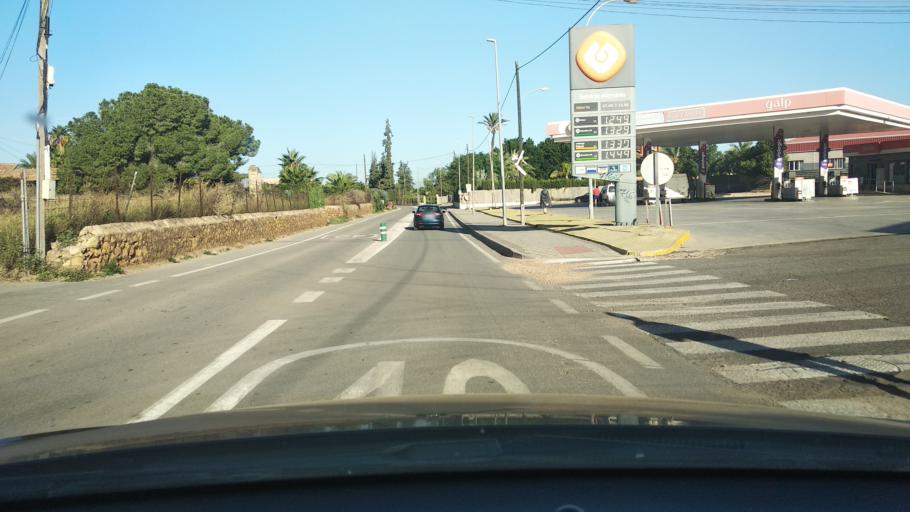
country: ES
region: Murcia
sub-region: Murcia
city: Murcia
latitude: 37.9430
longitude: -1.1184
